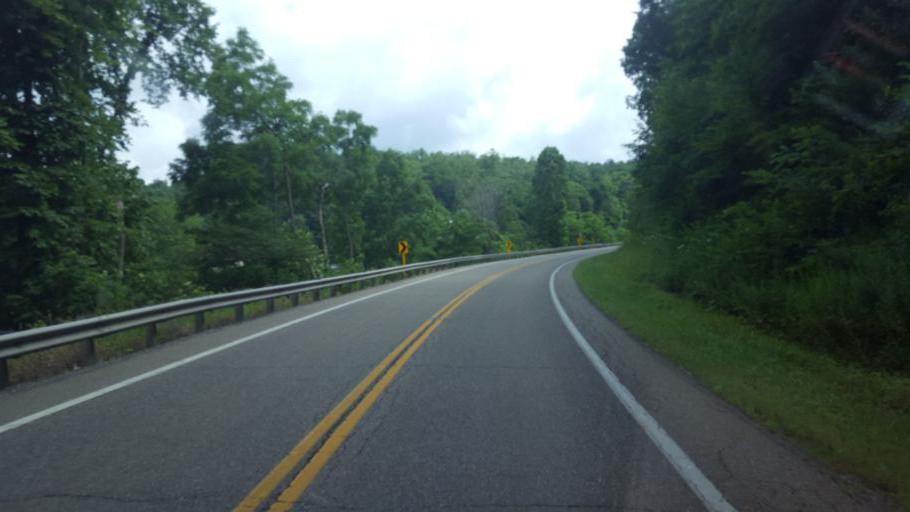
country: US
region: Ohio
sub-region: Columbiana County
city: Salineville
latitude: 40.6376
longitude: -80.8119
